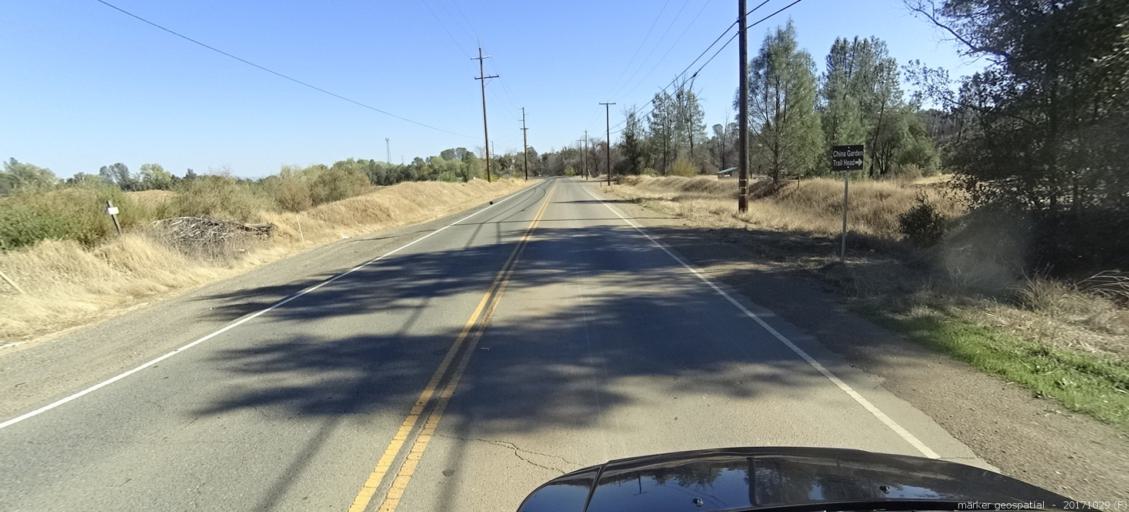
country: US
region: California
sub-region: Shasta County
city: Redding
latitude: 40.5075
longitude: -122.3974
